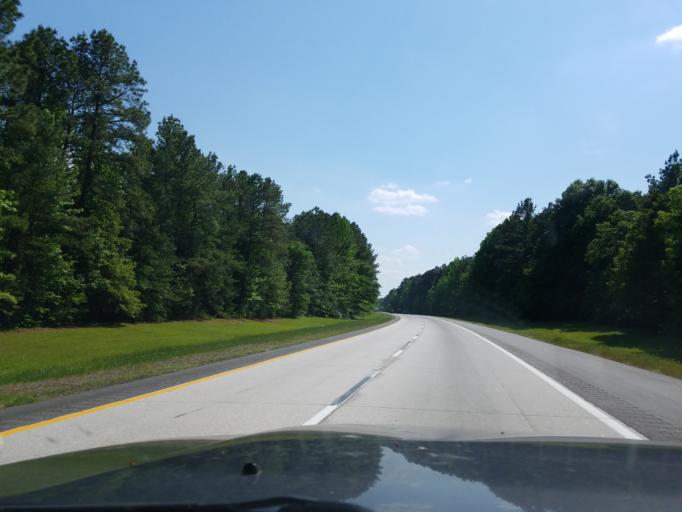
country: US
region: North Carolina
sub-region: Granville County
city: Creedmoor
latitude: 36.2086
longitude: -78.6767
